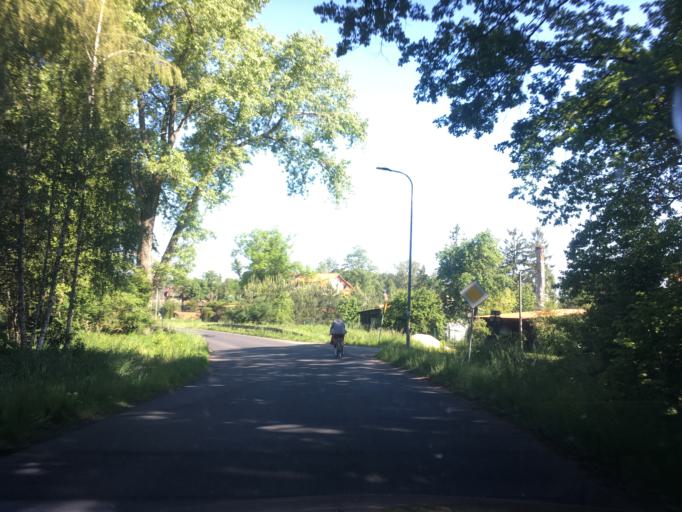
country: PL
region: Lower Silesian Voivodeship
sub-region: Powiat zgorzelecki
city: Zgorzelec
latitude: 51.1104
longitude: 15.0333
